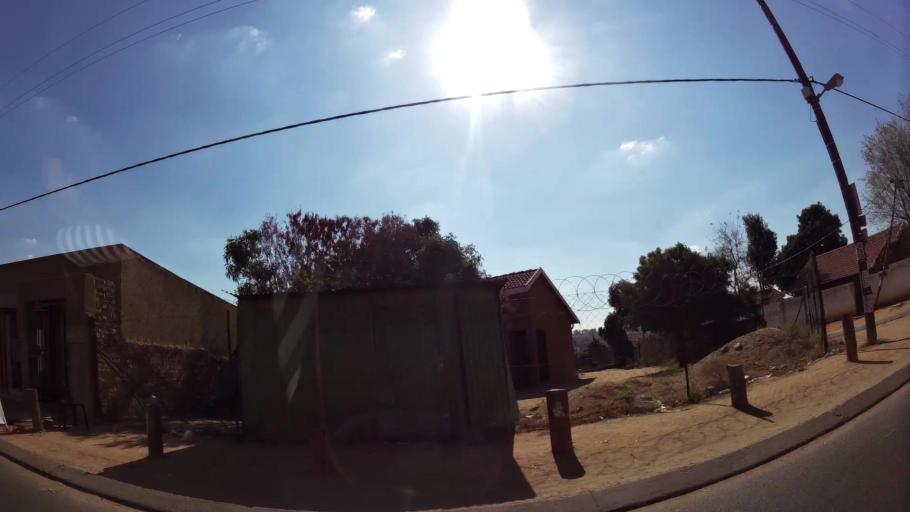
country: ZA
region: Gauteng
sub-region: West Rand District Municipality
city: Muldersdriseloop
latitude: -26.0172
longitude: 27.9368
